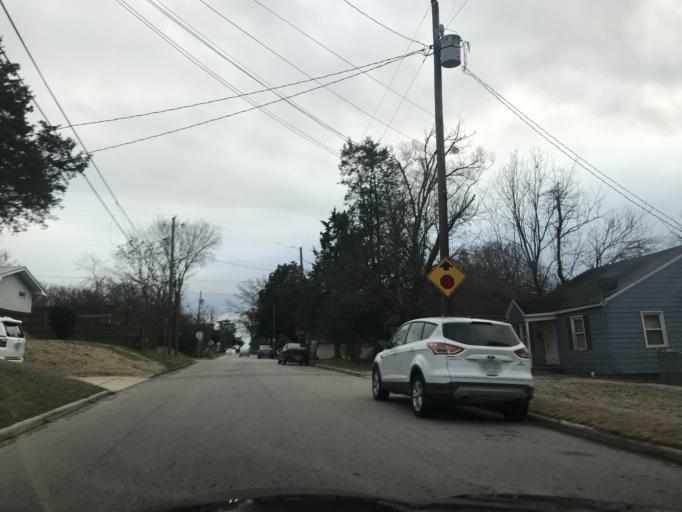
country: US
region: North Carolina
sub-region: Wake County
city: Raleigh
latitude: 35.7707
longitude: -78.6245
